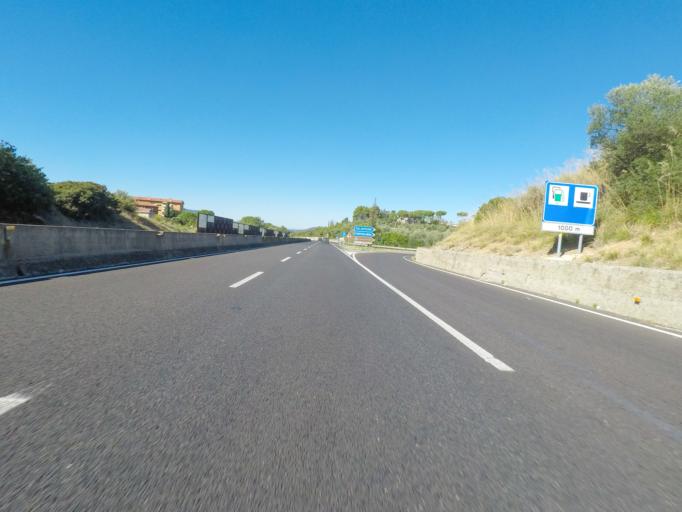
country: IT
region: Tuscany
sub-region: Provincia di Grosseto
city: Fonteblanda
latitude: 42.5654
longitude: 11.1730
